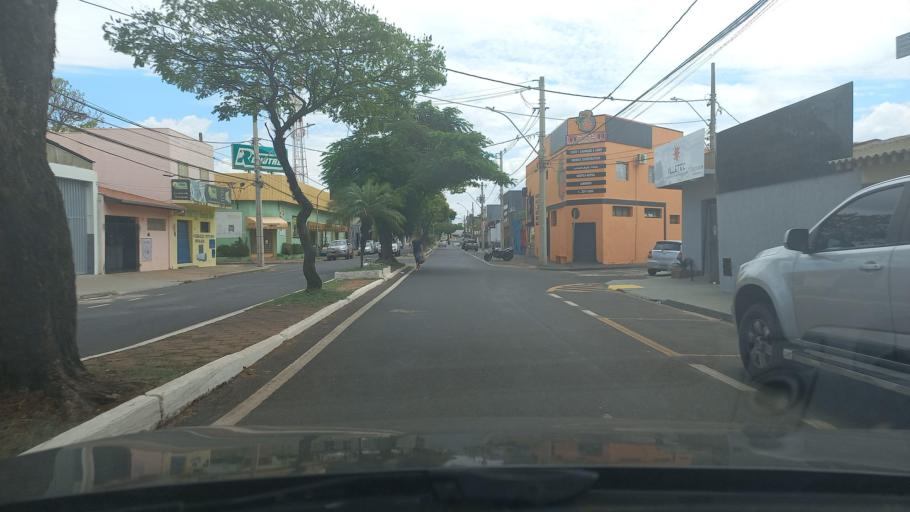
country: BR
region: Minas Gerais
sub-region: Uberaba
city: Uberaba
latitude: -19.7705
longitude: -47.9534
